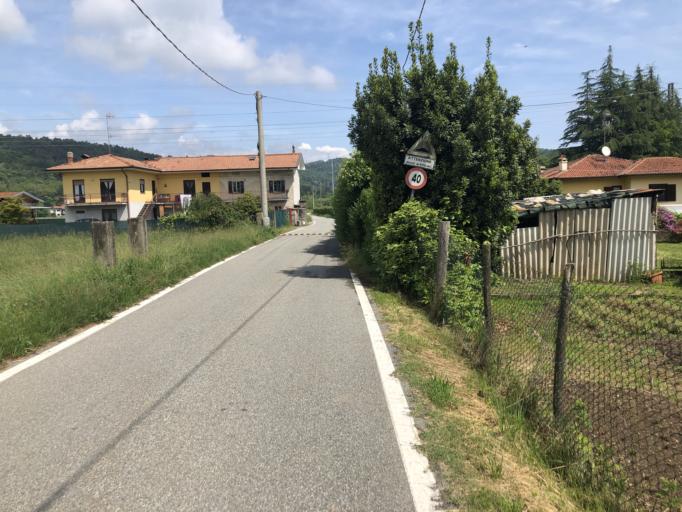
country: IT
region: Piedmont
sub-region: Provincia di Novara
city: Oleggio Castello
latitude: 45.7559
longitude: 8.5266
